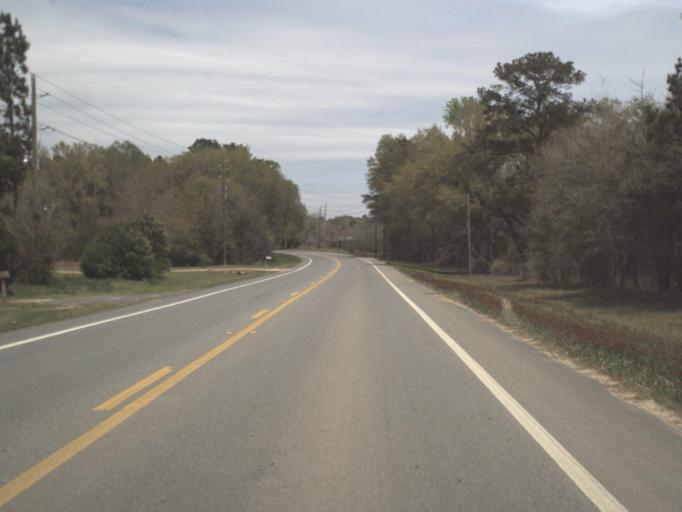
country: US
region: Florida
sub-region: Jackson County
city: Graceville
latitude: 30.9367
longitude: -85.4158
